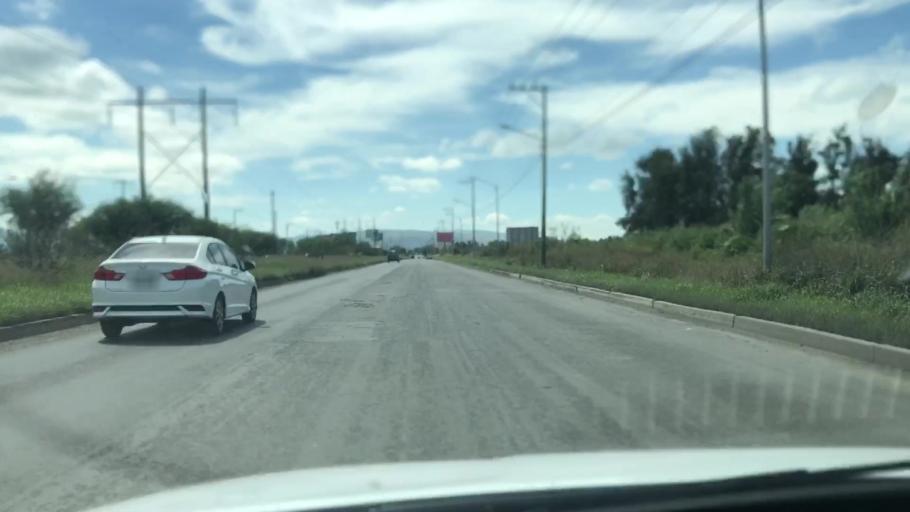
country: MX
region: Guanajuato
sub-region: Celaya
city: La Trinidad
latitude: 20.5428
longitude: -100.7798
